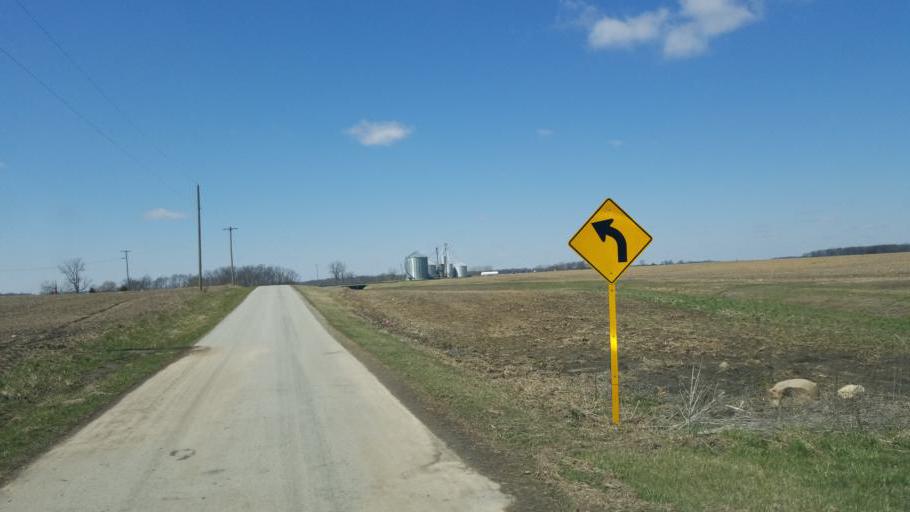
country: US
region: Ohio
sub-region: Wyandot County
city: Upper Sandusky
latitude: 40.7240
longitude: -83.1831
